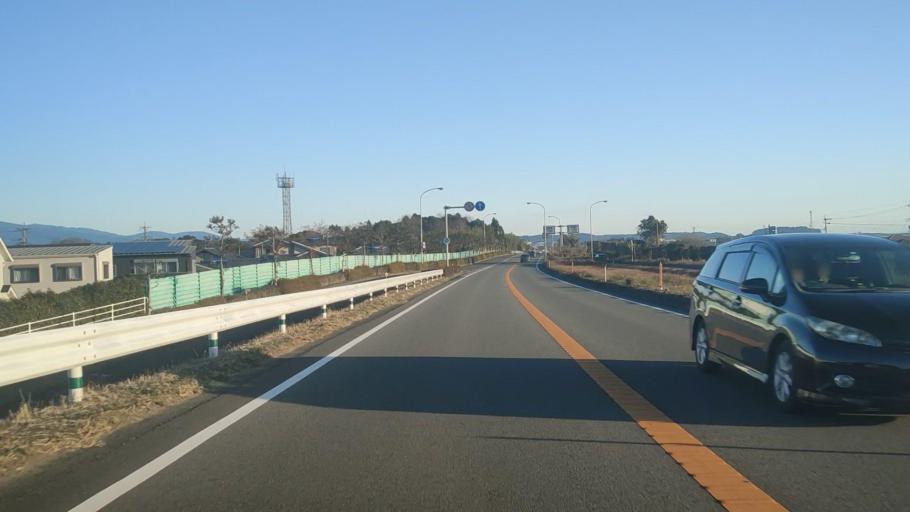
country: JP
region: Miyazaki
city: Tsuma
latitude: 32.0364
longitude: 131.4664
